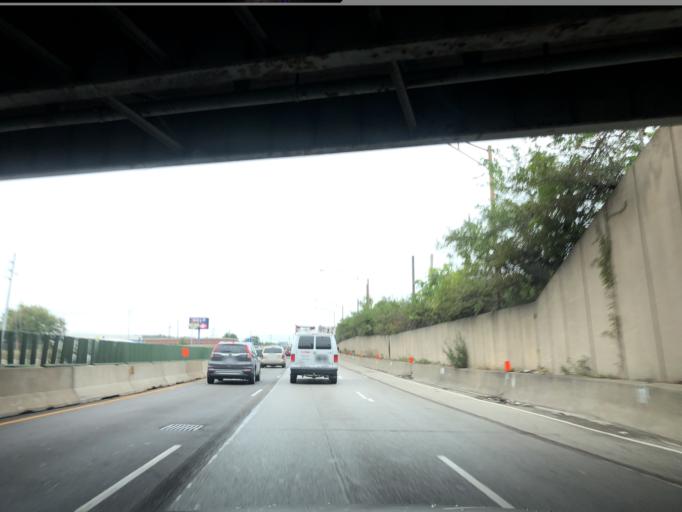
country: US
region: Ohio
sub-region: Hamilton County
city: Lincoln Heights
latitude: 39.2364
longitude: -84.4512
